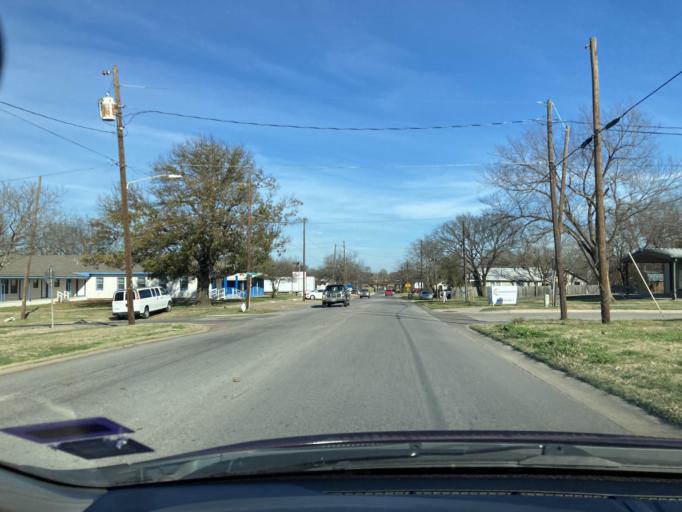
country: US
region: Texas
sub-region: Navarro County
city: Corsicana
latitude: 32.0985
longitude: -96.4658
